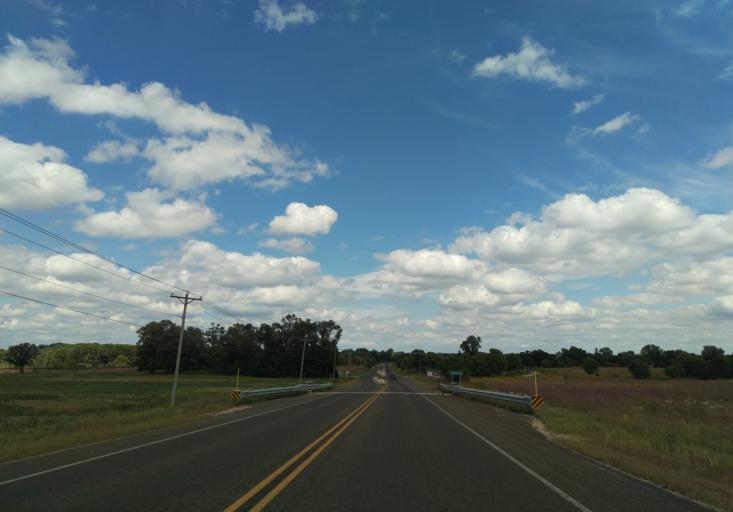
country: US
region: Wisconsin
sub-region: Dane County
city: Shorewood Hills
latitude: 43.1349
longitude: -89.4420
